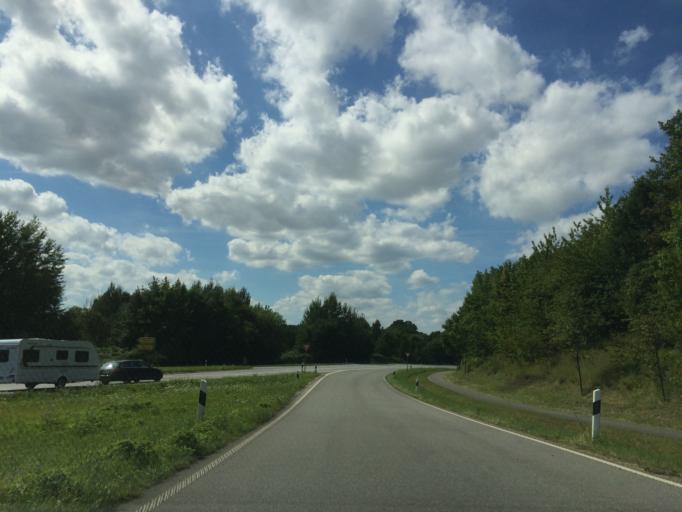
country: DE
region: Schleswig-Holstein
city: Eutin
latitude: 54.1288
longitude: 10.5758
